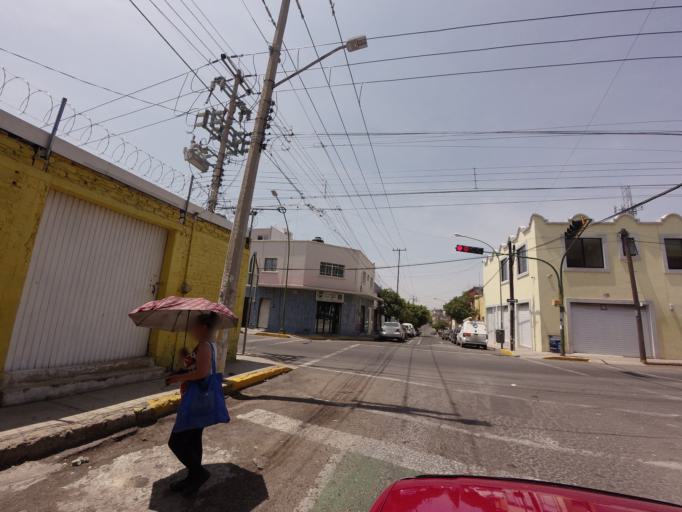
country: MX
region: Jalisco
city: Guadalajara
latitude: 20.6849
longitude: -103.3435
